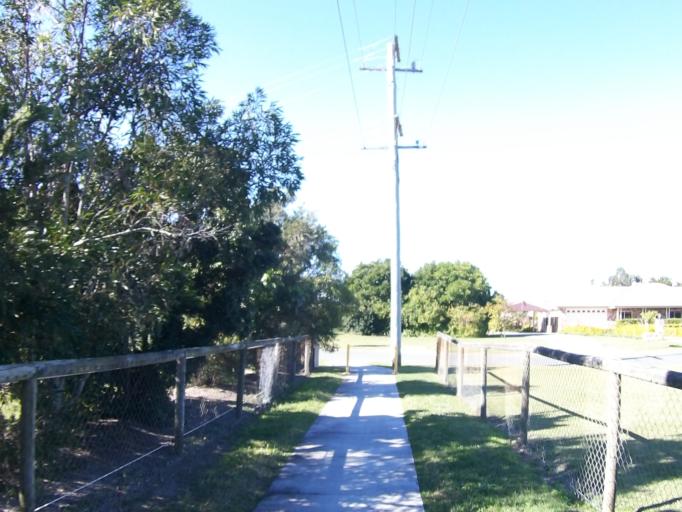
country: AU
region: Queensland
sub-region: Logan
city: Windaroo
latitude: -27.7475
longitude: 153.2064
